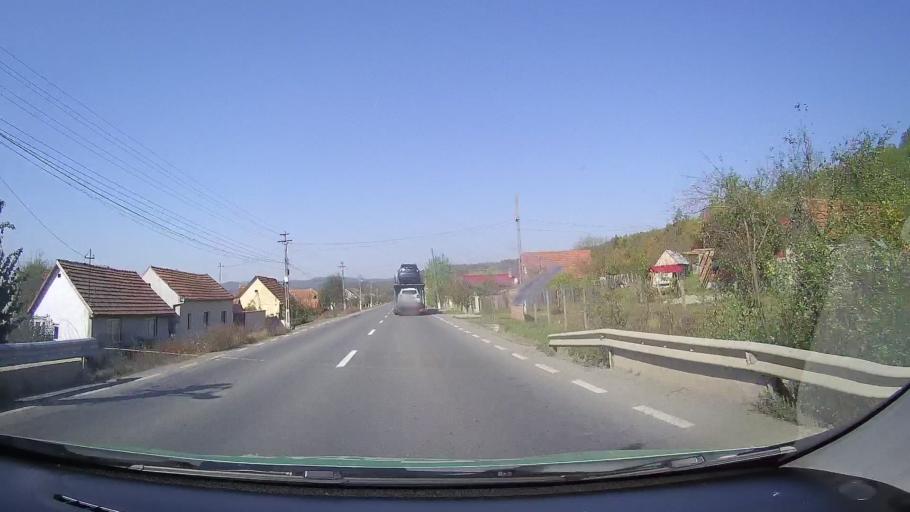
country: RO
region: Arad
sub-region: Comuna Barzava
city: Barzava
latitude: 46.0909
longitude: 22.0227
